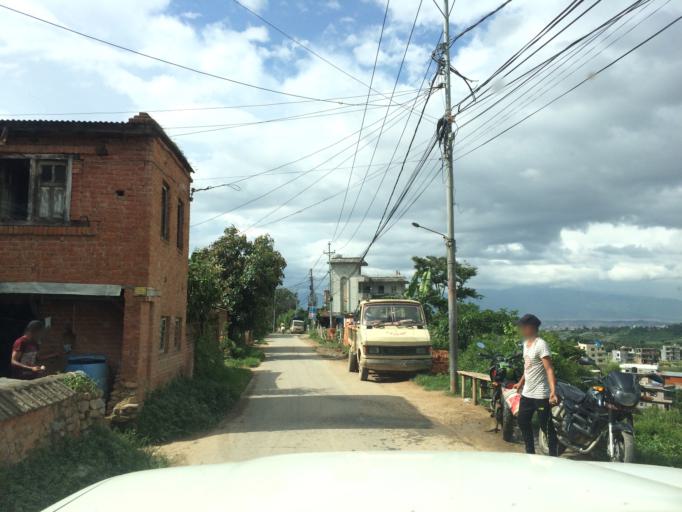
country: NP
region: Central Region
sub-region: Bagmati Zone
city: Patan
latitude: 27.6216
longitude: 85.3046
